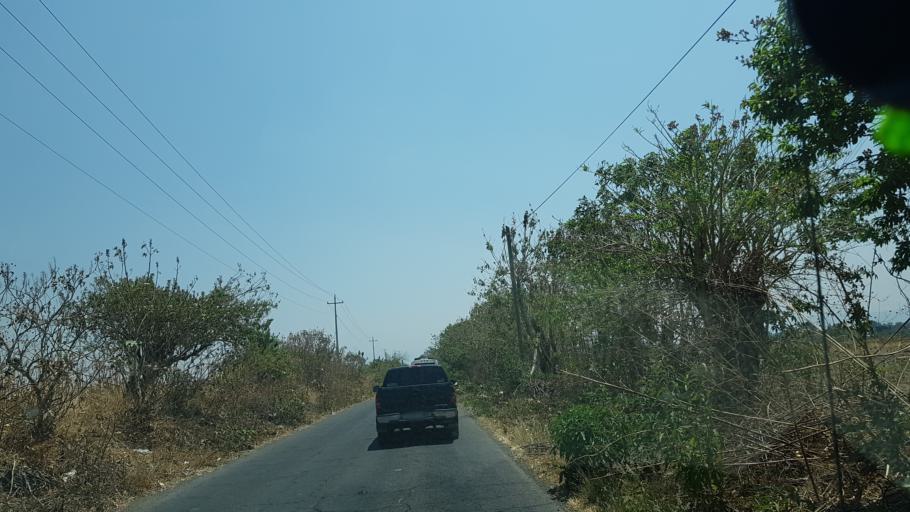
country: MX
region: Puebla
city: Tochimilco
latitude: 18.8897
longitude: -98.5242
